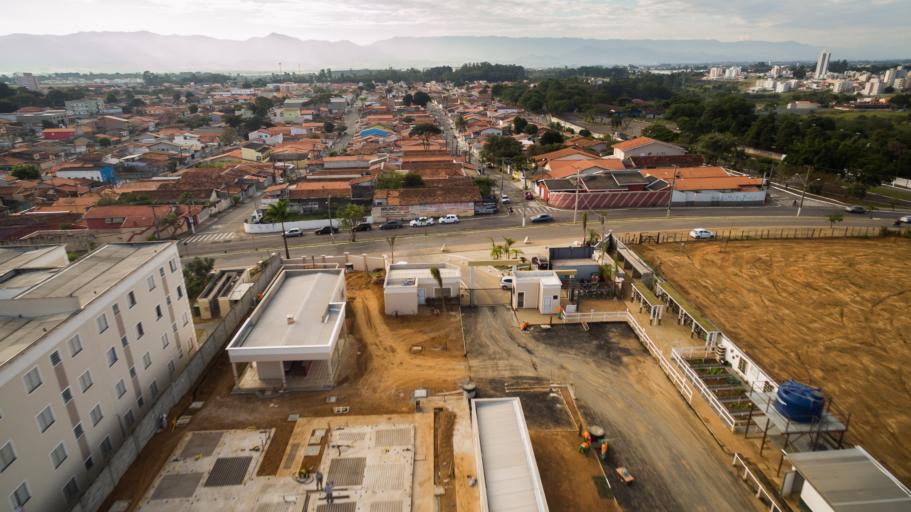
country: BR
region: Sao Paulo
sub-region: Taubate
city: Taubate
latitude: -23.0375
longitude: -45.6008
